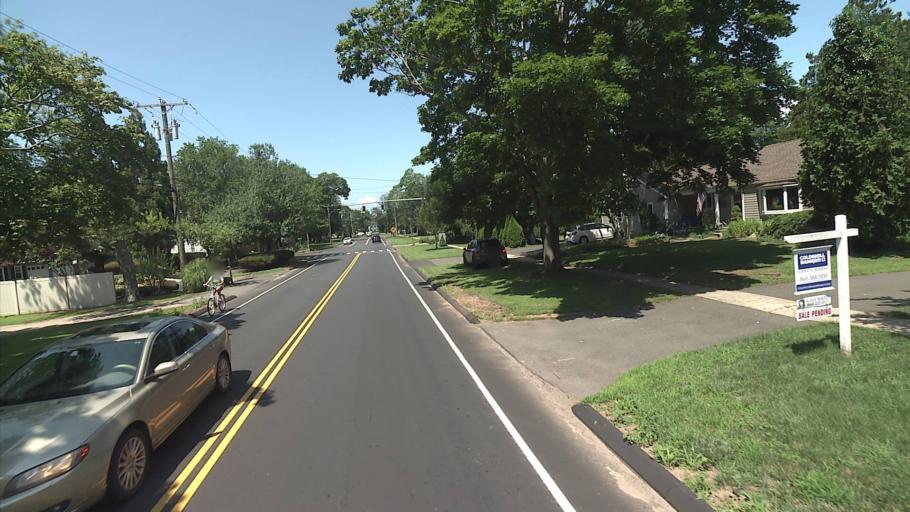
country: US
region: Connecticut
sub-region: Middlesex County
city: Old Saybrook
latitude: 41.2839
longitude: -72.3713
